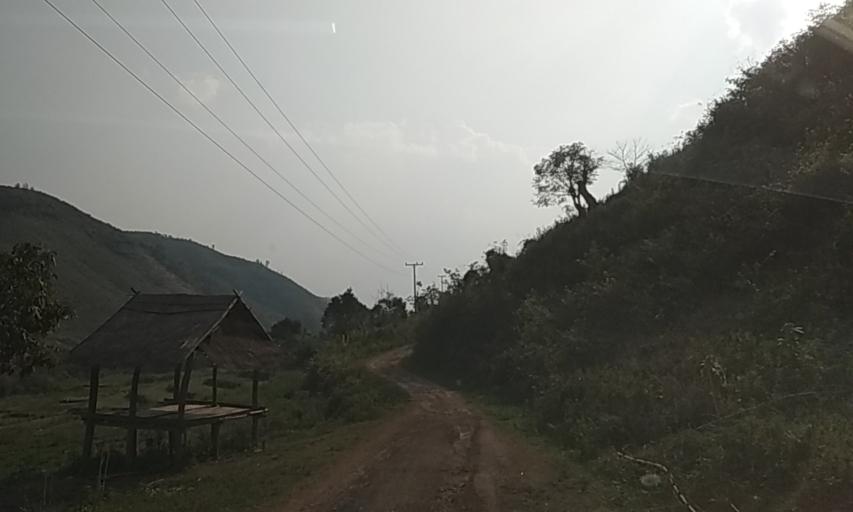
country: LA
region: Louangphabang
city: Louangphabang
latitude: 20.0336
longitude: 101.7916
